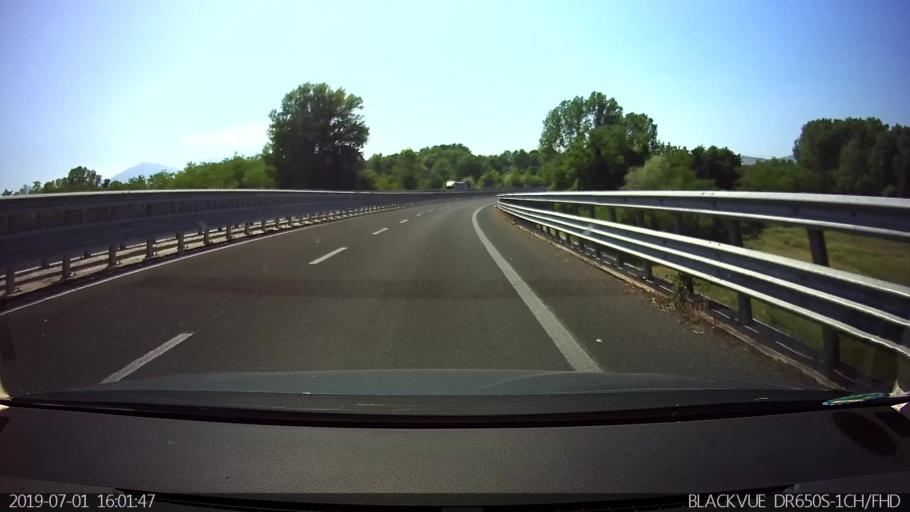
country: IT
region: Latium
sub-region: Provincia di Frosinone
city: Castelmassimo
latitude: 41.6624
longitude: 13.3656
